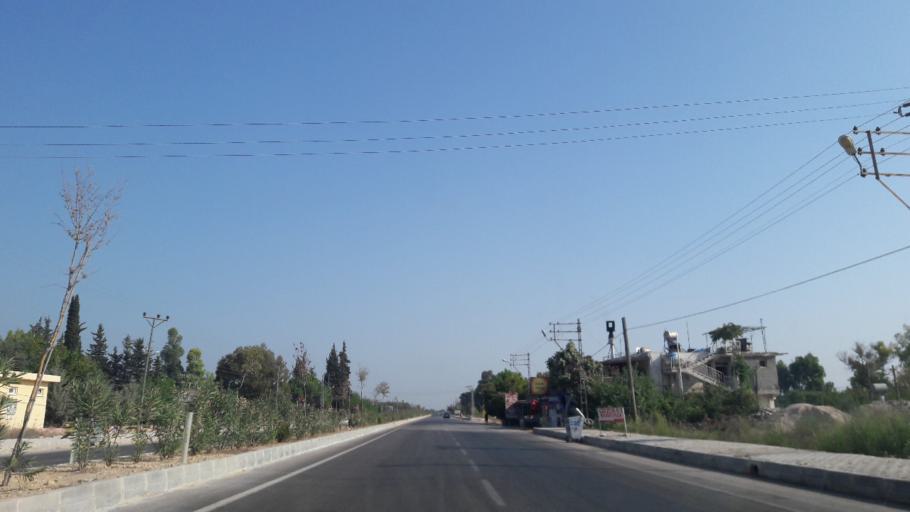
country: TR
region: Adana
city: Yakapinar
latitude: 37.1109
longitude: 35.5113
